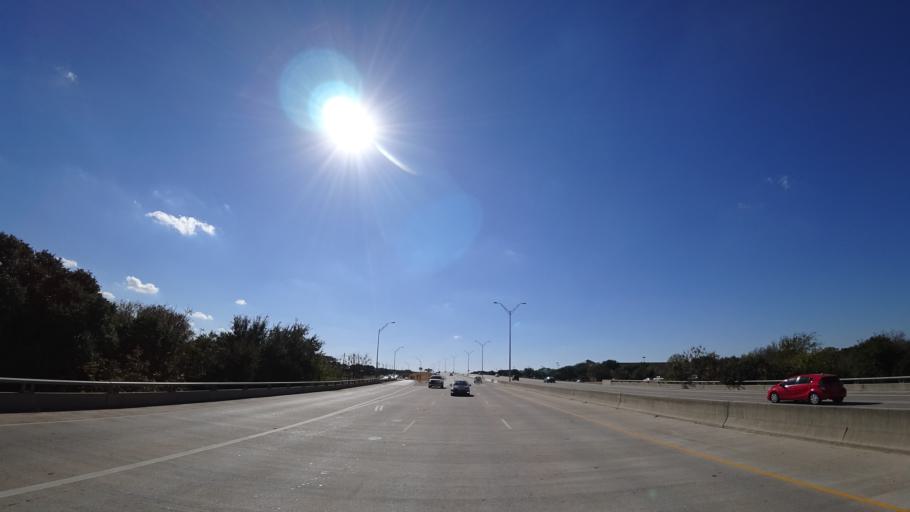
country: US
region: Texas
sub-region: Travis County
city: Shady Hollow
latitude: 30.2239
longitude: -97.8334
